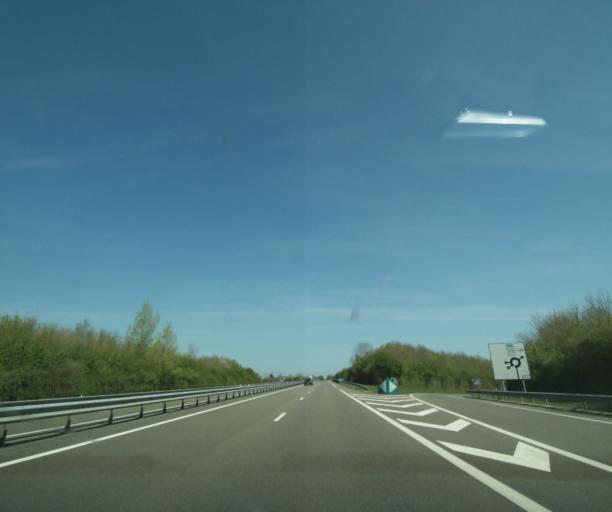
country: FR
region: Bourgogne
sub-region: Departement de la Nievre
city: Saint-Eloi
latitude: 46.9771
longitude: 3.1997
